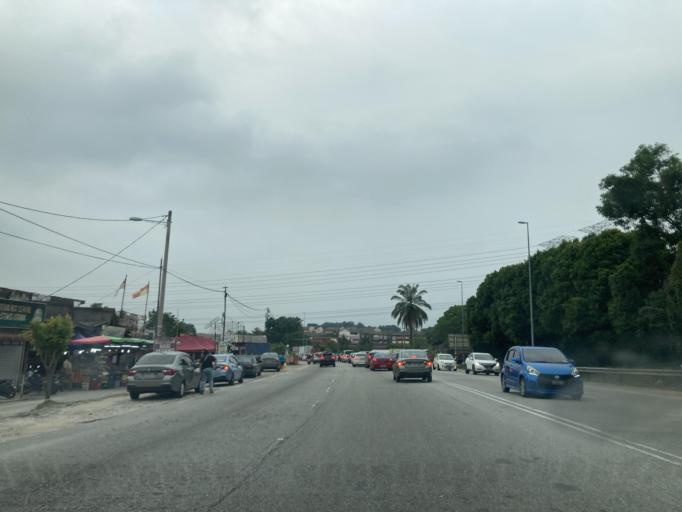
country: MY
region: Selangor
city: Kampung Baru Subang
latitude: 3.2028
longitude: 101.5465
